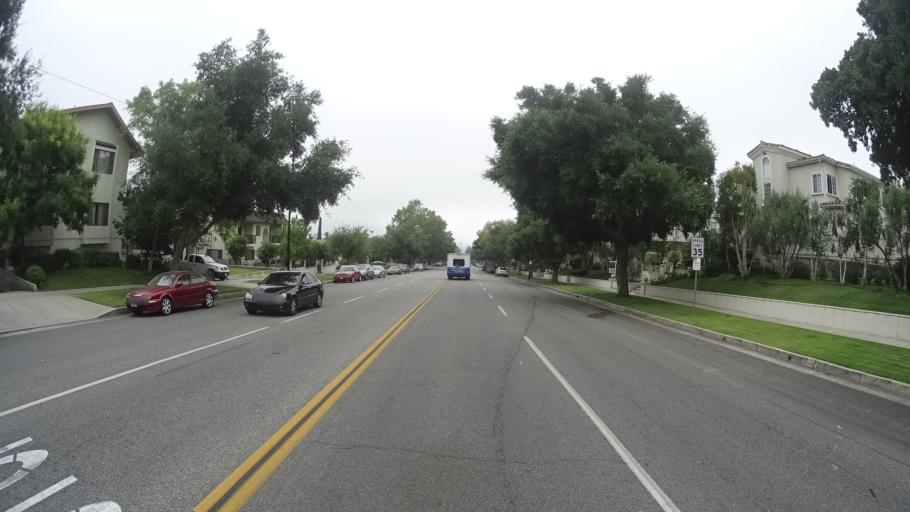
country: US
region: California
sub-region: Los Angeles County
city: Burbank
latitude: 34.1877
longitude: -118.3015
